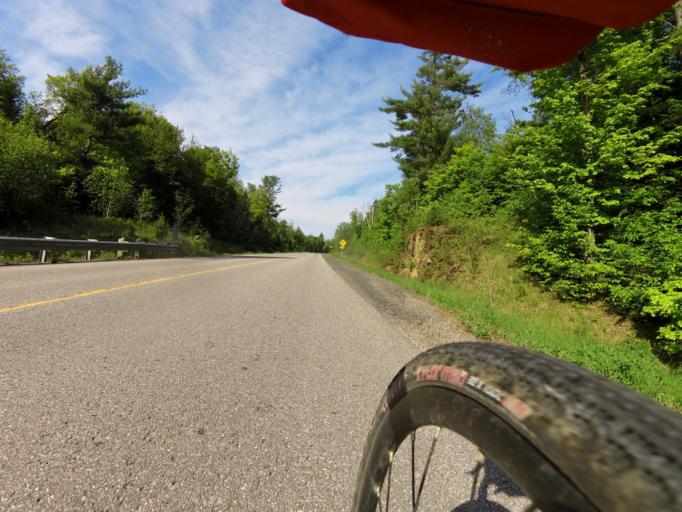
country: CA
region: Ontario
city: Arnprior
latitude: 45.1686
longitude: -76.4953
